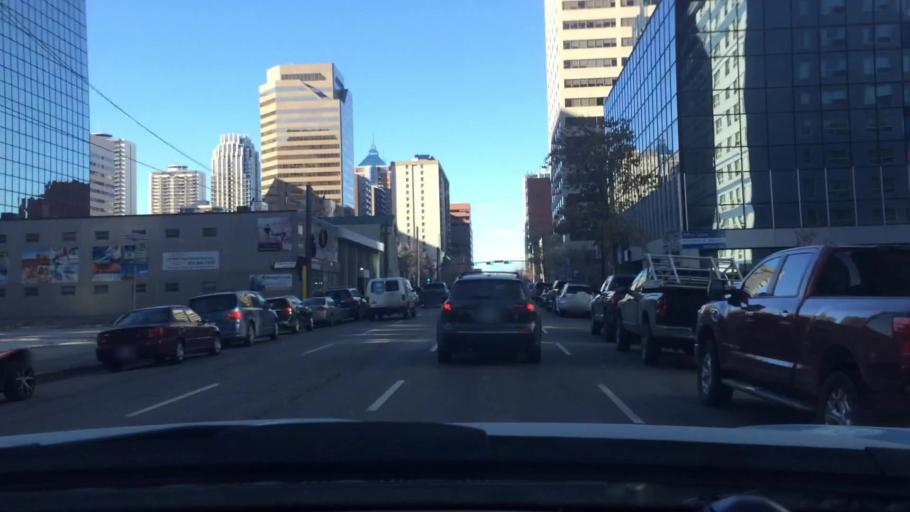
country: CA
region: Alberta
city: Calgary
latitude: 51.0497
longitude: -114.0740
